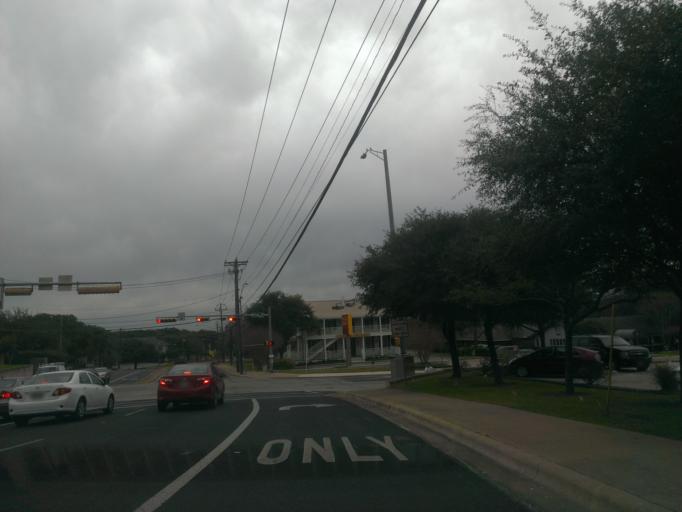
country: US
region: Texas
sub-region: Williamson County
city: Jollyville
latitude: 30.3716
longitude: -97.7577
